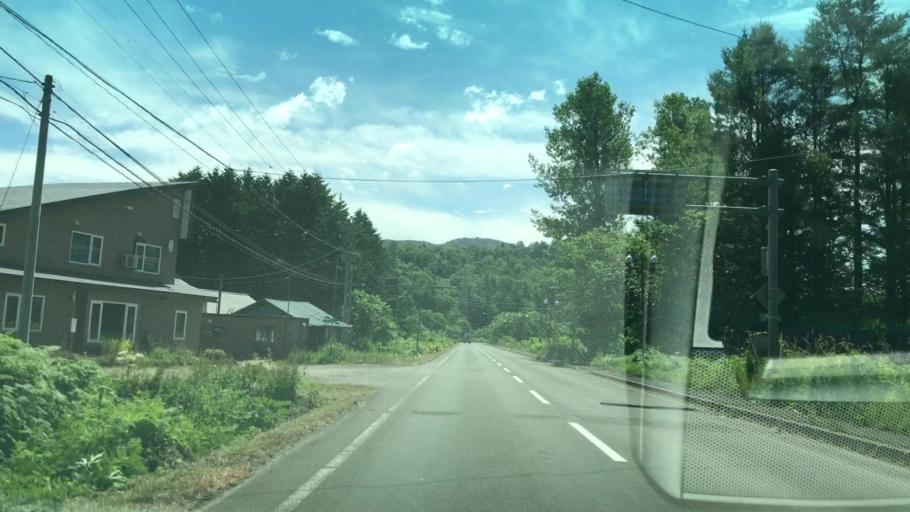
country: JP
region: Hokkaido
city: Shimo-furano
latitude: 42.9514
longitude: 142.4385
